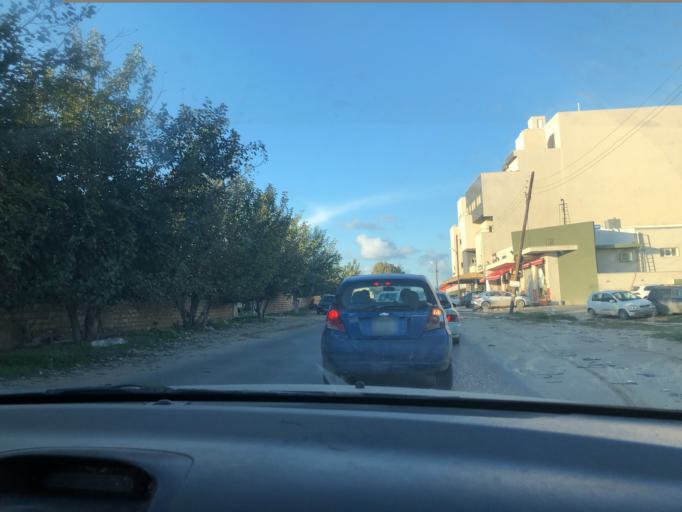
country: LY
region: Tripoli
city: Tagiura
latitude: 32.8576
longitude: 13.2789
